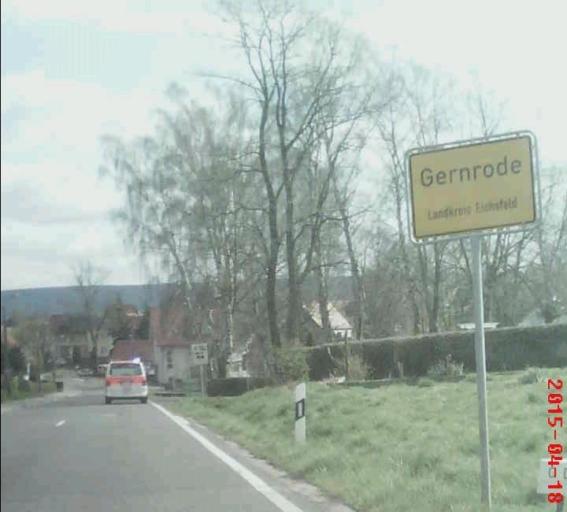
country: DE
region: Thuringia
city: Kirchworbis
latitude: 51.3988
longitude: 10.3974
